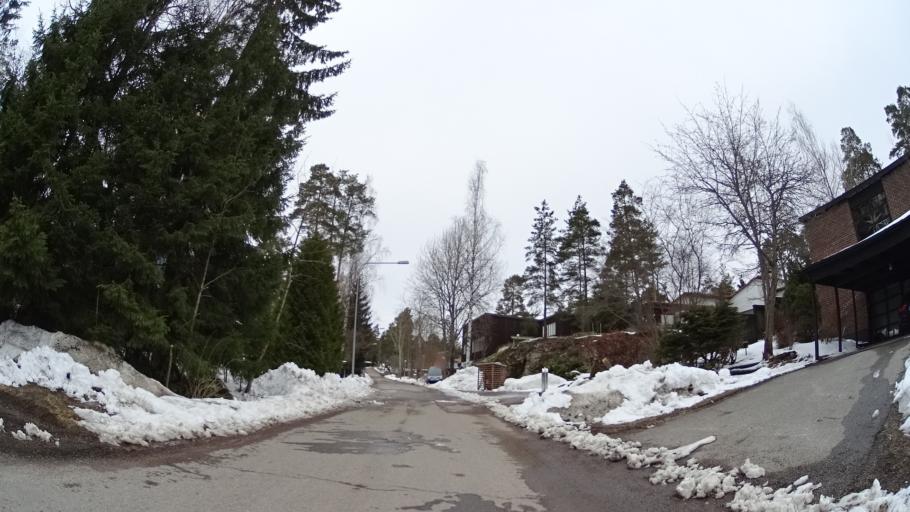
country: FI
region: Uusimaa
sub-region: Helsinki
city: Kauniainen
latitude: 60.2118
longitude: 24.7154
